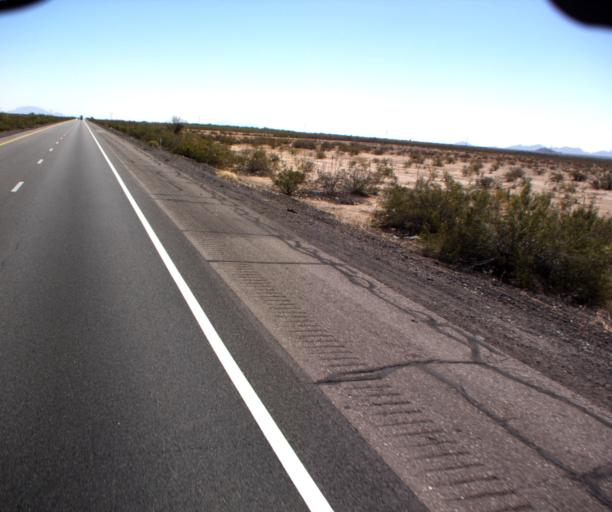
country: US
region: Arizona
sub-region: La Paz County
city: Salome
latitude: 33.5812
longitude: -113.4359
